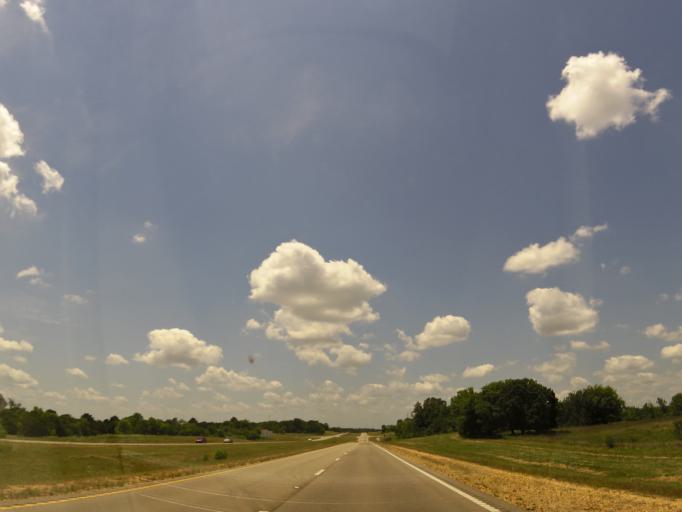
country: US
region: Mississippi
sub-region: Lee County
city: Verona
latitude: 34.2133
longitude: -88.7922
